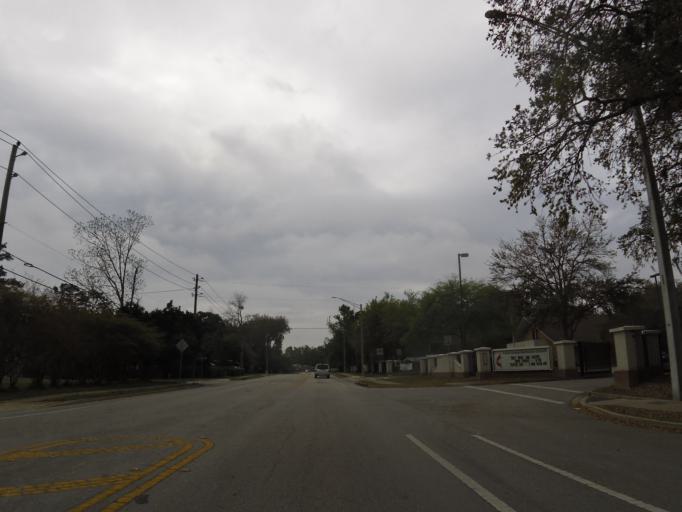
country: US
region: Florida
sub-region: Duval County
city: Jacksonville
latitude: 30.2852
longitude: -81.6207
